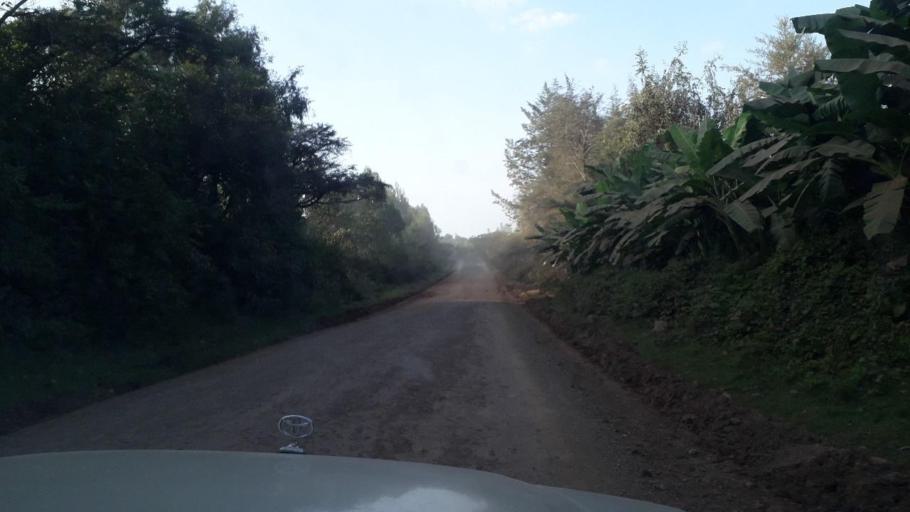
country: ET
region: Oromiya
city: Jima
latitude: 7.5856
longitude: 36.8573
